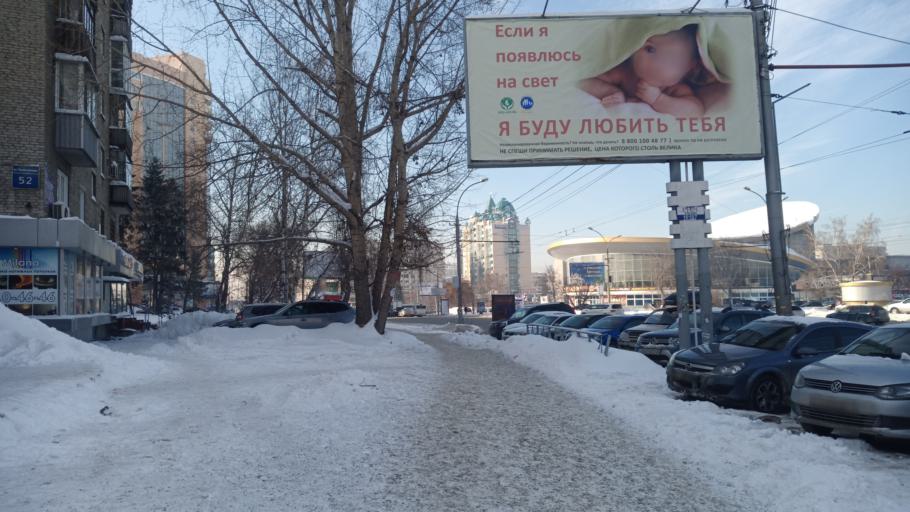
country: RU
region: Novosibirsk
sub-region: Novosibirskiy Rayon
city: Novosibirsk
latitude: 55.0417
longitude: 82.9130
